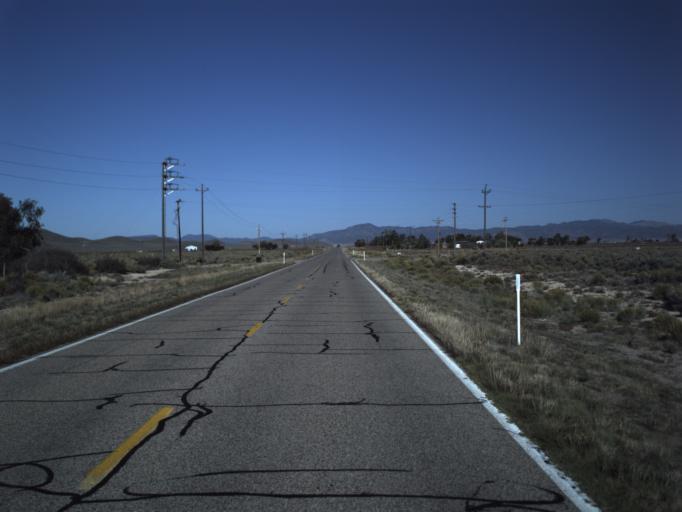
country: US
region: Utah
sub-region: Washington County
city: Enterprise
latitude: 37.7220
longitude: -113.6911
